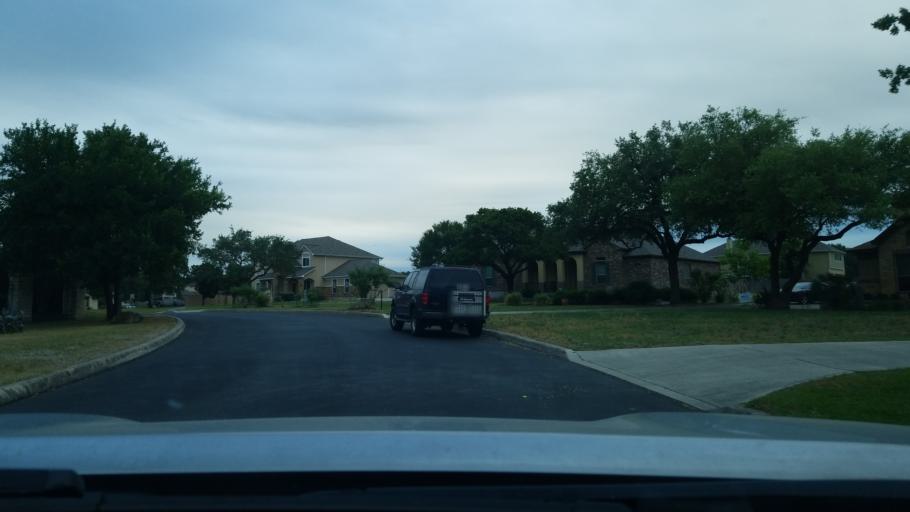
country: US
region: Texas
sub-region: Bexar County
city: Timberwood Park
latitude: 29.7142
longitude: -98.4966
